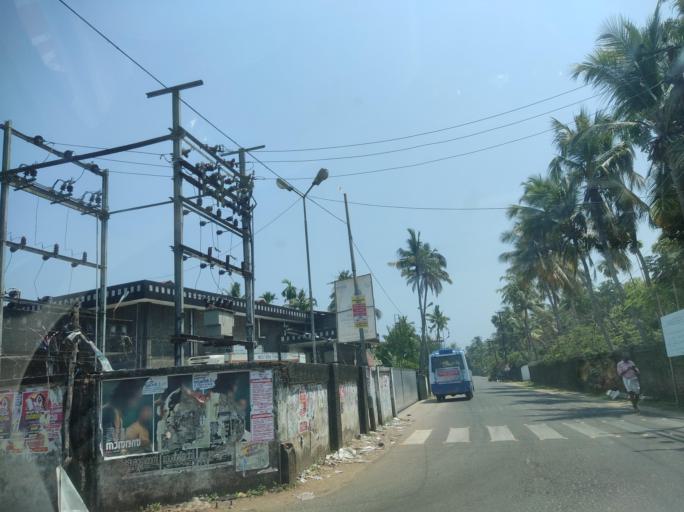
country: IN
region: Kerala
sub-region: Alappuzha
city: Kutiatodu
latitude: 9.8211
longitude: 76.2986
